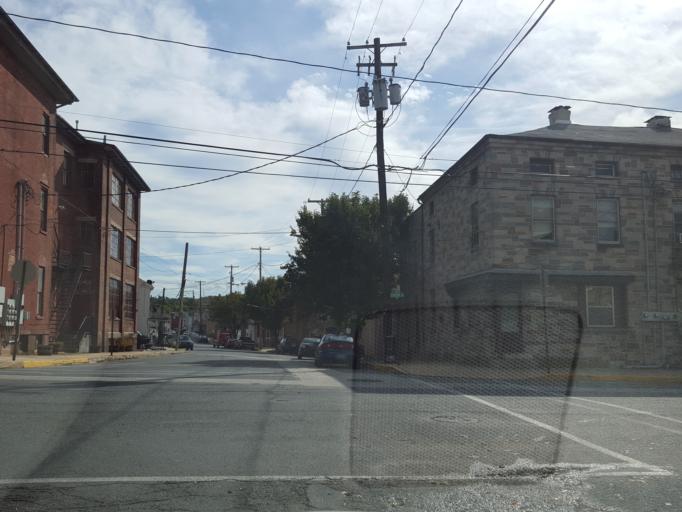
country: US
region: Pennsylvania
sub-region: Lancaster County
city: Columbia
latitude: 40.0301
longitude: -76.5006
